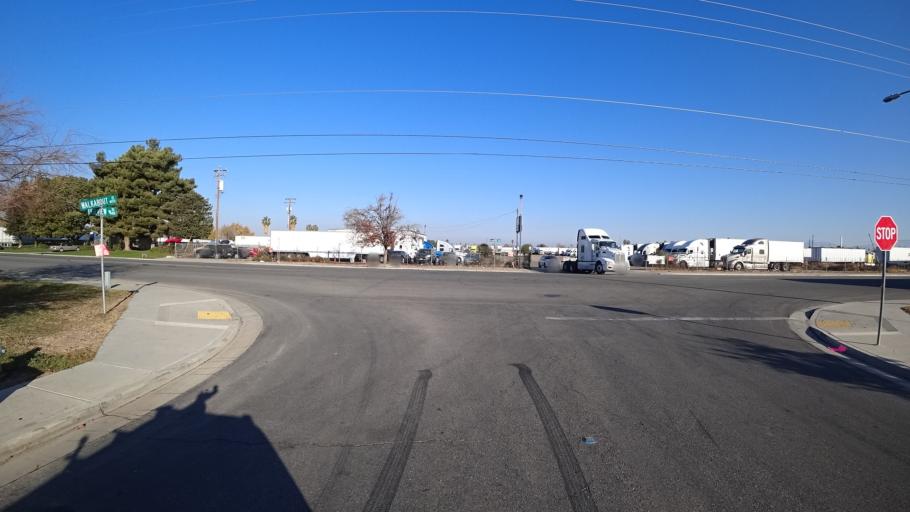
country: US
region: California
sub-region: Kern County
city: Greenfield
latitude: 35.3030
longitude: -119.0060
